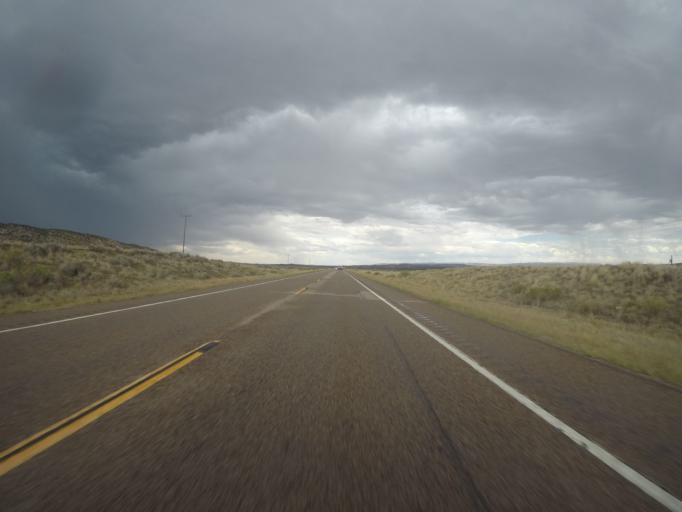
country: US
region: Colorado
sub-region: Rio Blanco County
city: Rangely
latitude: 40.2397
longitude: -108.9240
